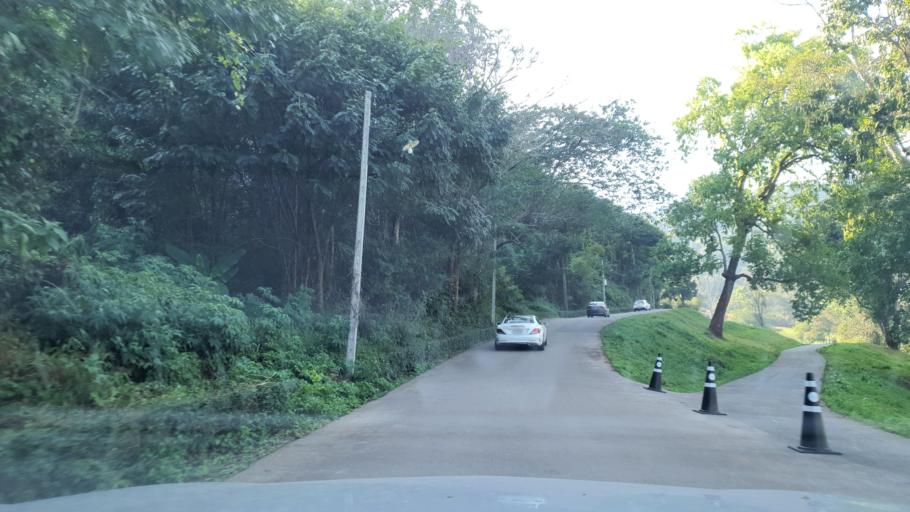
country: TH
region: Chiang Mai
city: Samoeng
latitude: 18.9004
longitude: 98.8263
